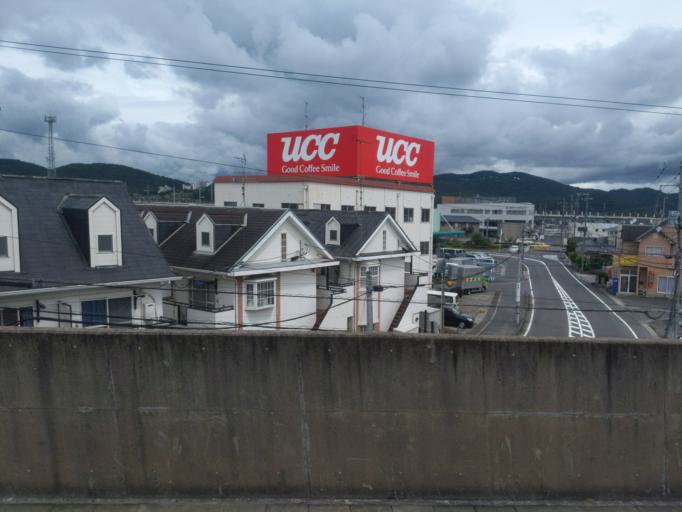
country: JP
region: Okayama
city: Okayama-shi
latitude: 34.6793
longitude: 133.9395
